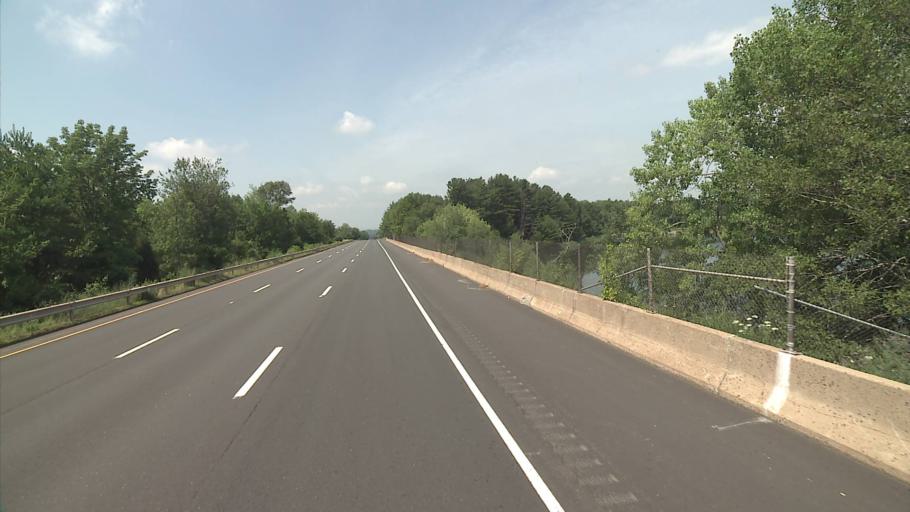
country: US
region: Connecticut
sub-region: Hartford County
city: Manchester
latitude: 41.7702
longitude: -72.4751
